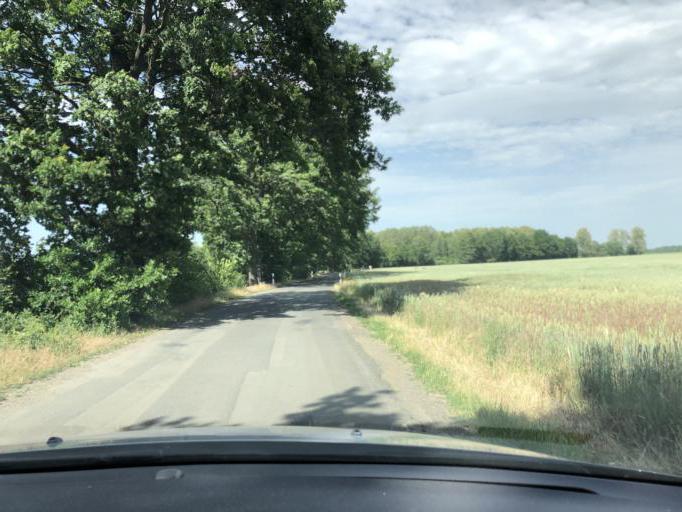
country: DE
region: Saxony
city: Borsdorf
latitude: 51.3265
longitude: 12.5498
